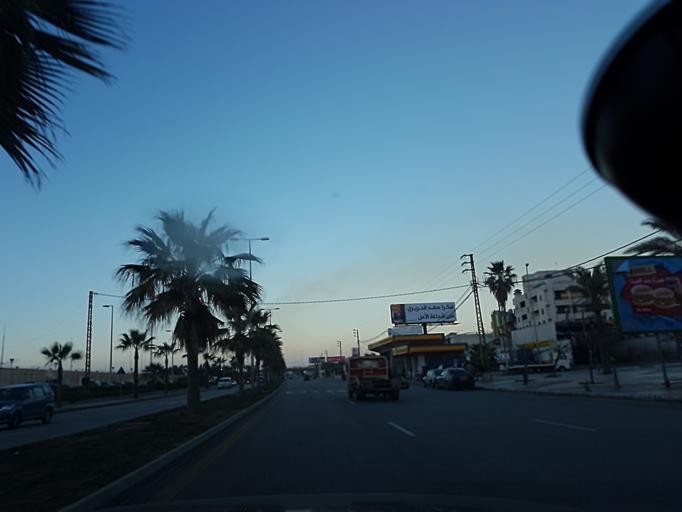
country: LB
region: Liban-Sud
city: Sidon
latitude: 33.5835
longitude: 35.3856
